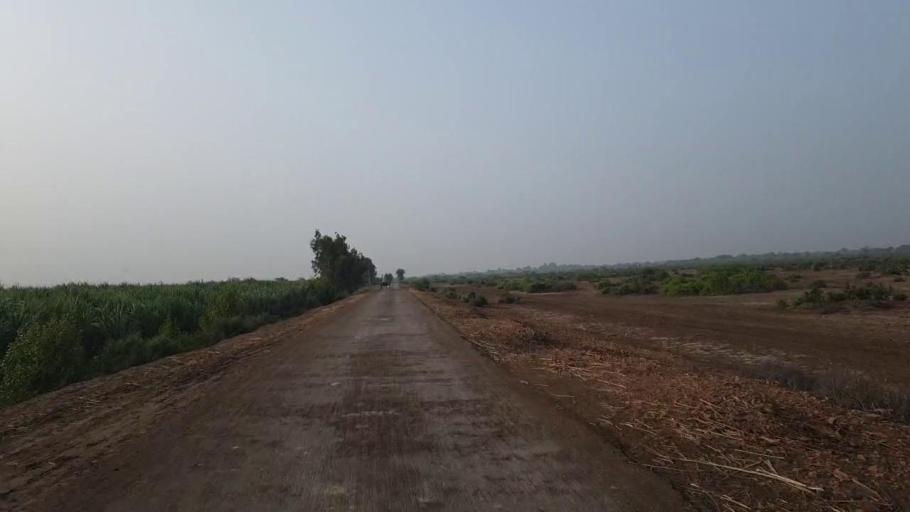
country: PK
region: Sindh
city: Tando Muhammad Khan
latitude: 25.1549
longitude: 68.6095
